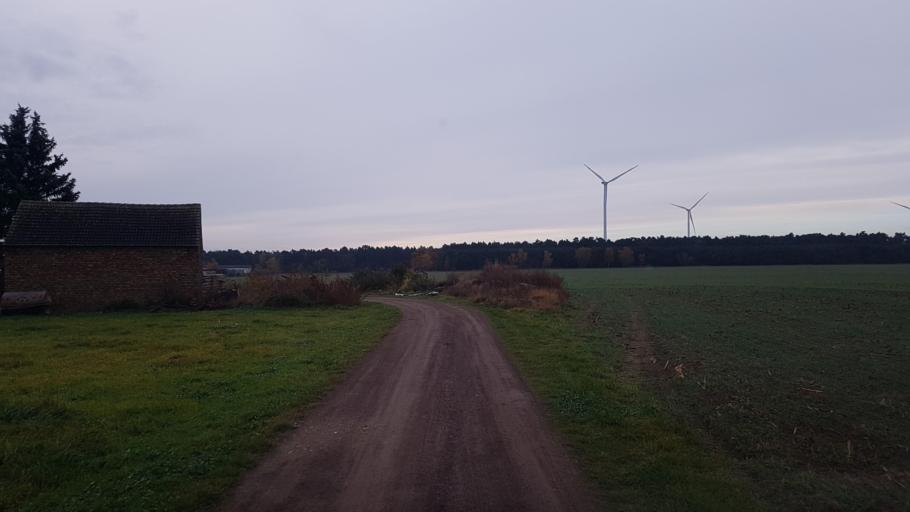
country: DE
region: Saxony-Anhalt
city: Seyda
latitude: 51.9243
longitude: 12.8853
